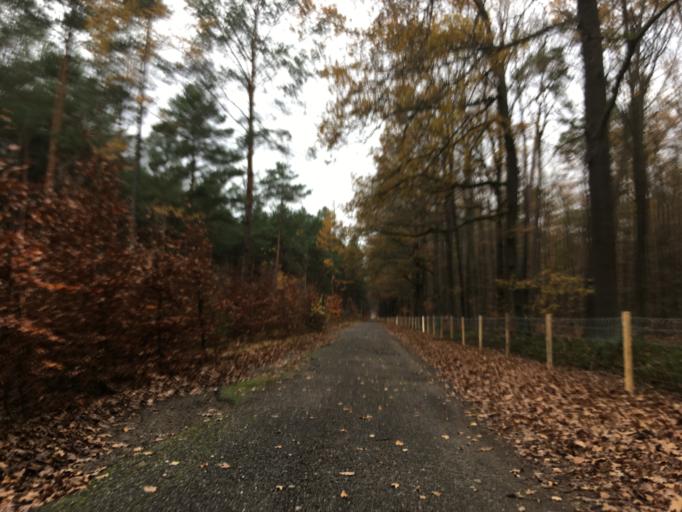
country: DE
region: Brandenburg
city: Jamlitz
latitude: 52.0726
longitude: 14.4808
